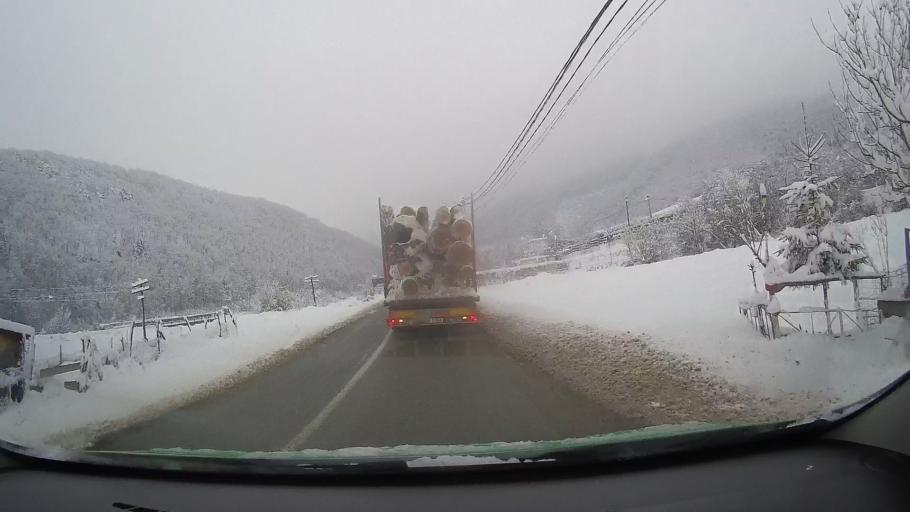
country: RO
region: Sibiu
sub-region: Comuna Orlat
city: Orlat
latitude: 45.7655
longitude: 23.9401
